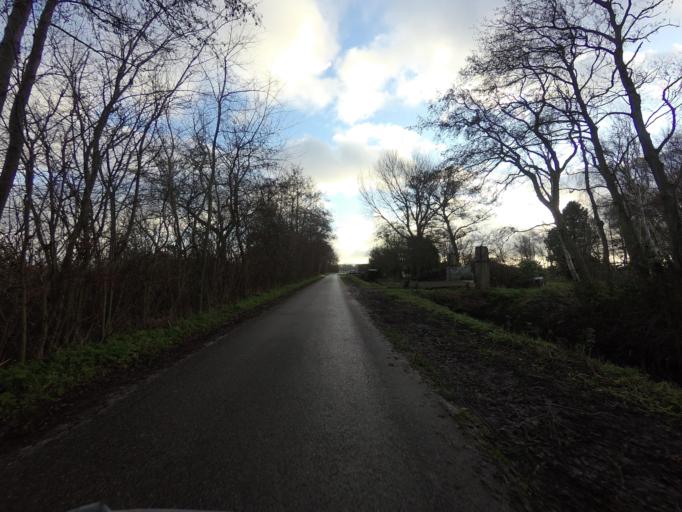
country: NL
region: North Holland
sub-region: Gemeente Texel
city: Den Burg
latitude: 53.0935
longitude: 4.7746
